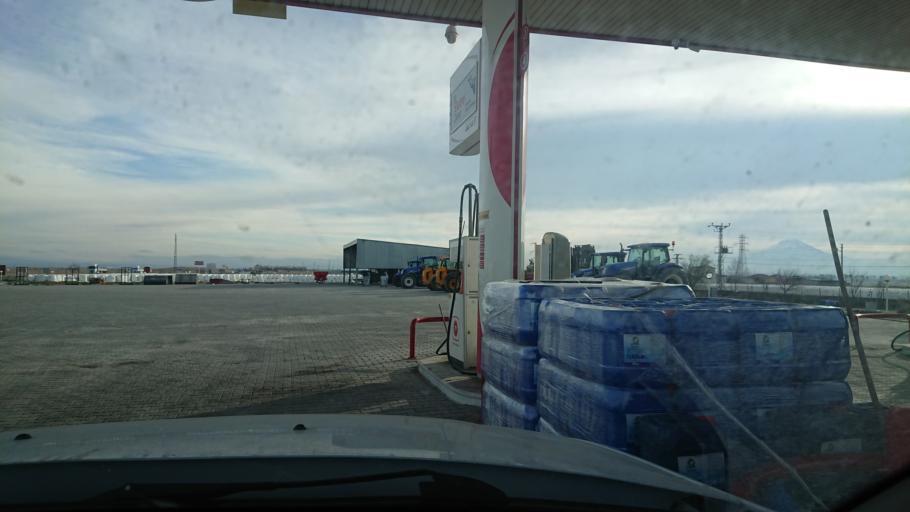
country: TR
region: Aksaray
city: Yesilova
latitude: 38.2923
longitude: 33.7673
